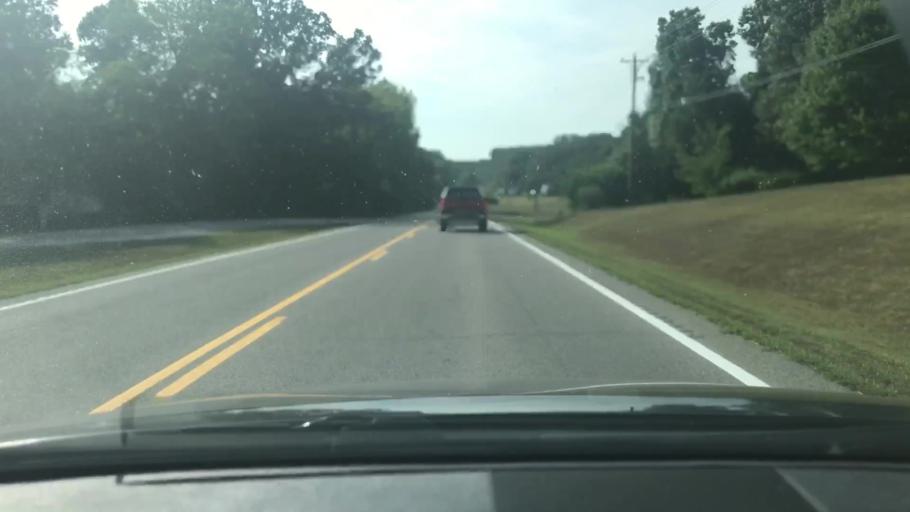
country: US
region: Tennessee
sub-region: Williamson County
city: Fairview
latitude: 36.0123
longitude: -87.1503
